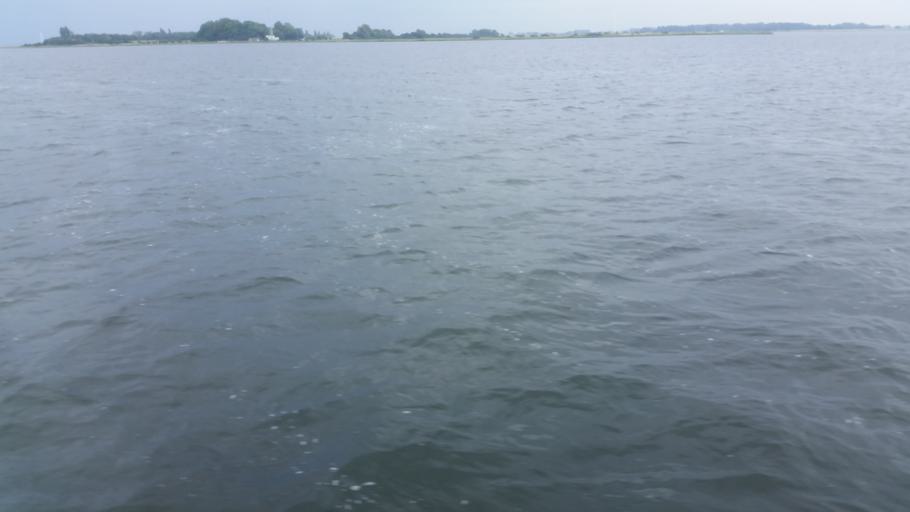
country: DE
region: Mecklenburg-Vorpommern
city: Hiddensee
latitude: 54.5431
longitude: 13.1314
